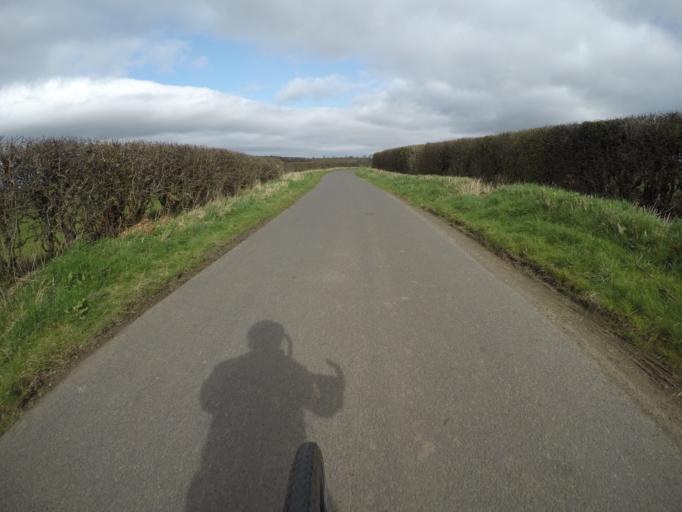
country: GB
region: Scotland
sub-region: North Ayrshire
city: Irvine
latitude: 55.6391
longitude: -4.6297
